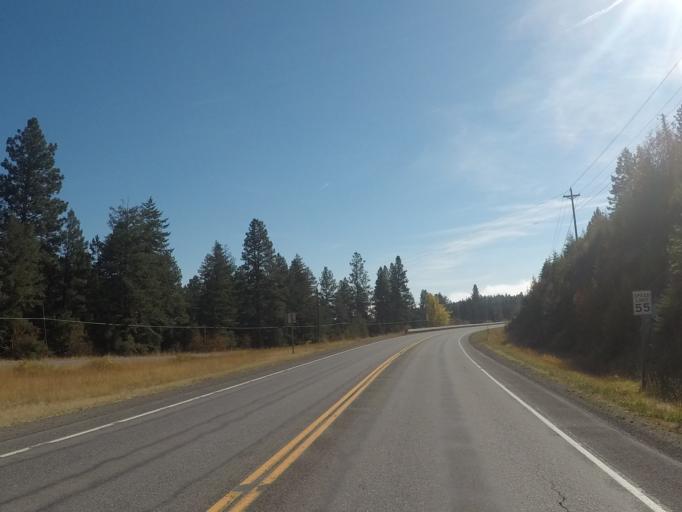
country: US
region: Montana
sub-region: Flathead County
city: Somers
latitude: 48.0545
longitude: -114.2358
